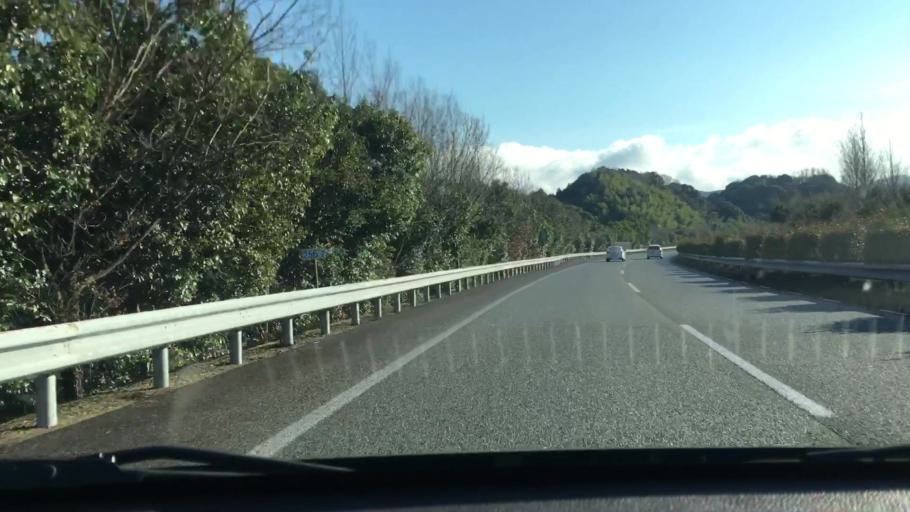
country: JP
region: Kumamoto
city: Hitoyoshi
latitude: 32.1965
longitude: 130.7777
